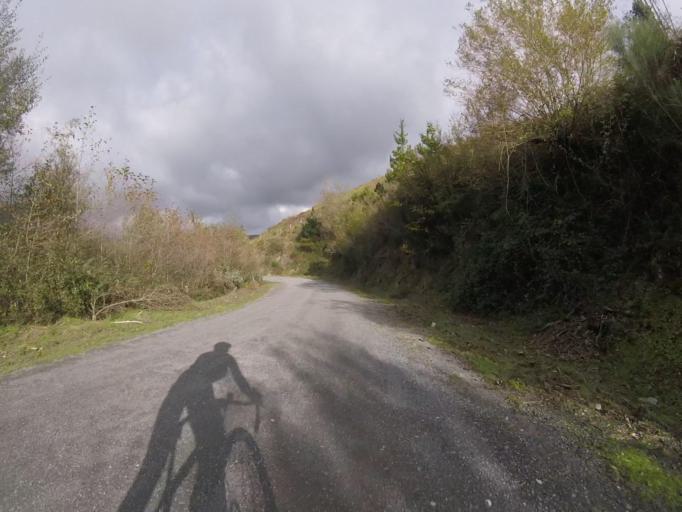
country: ES
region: Navarre
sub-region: Provincia de Navarra
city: Goizueta
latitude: 43.2100
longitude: -1.8318
